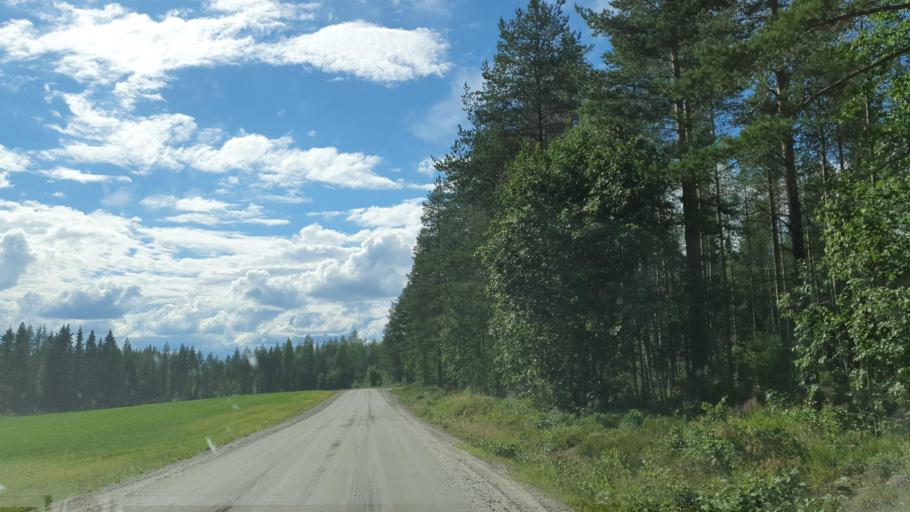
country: FI
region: Kainuu
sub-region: Kehys-Kainuu
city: Kuhmo
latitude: 64.1397
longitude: 29.6881
